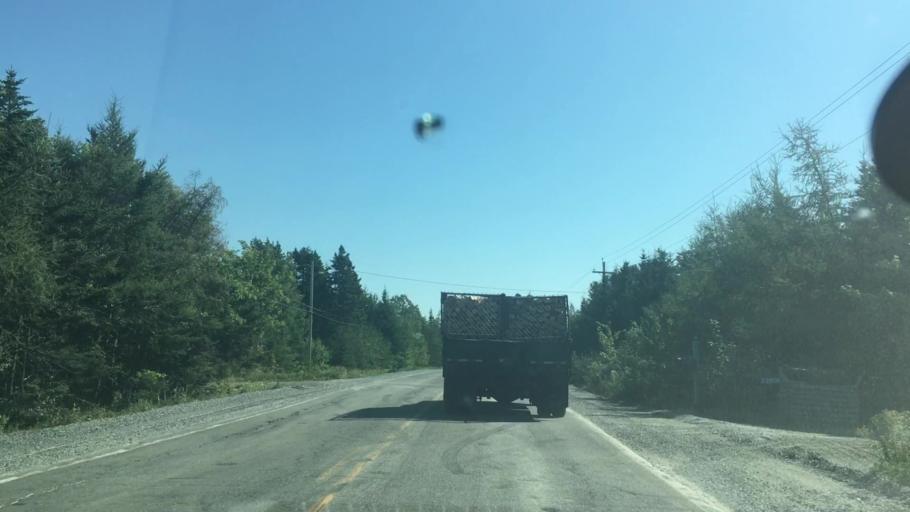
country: CA
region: Nova Scotia
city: New Glasgow
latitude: 44.9040
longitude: -62.4624
